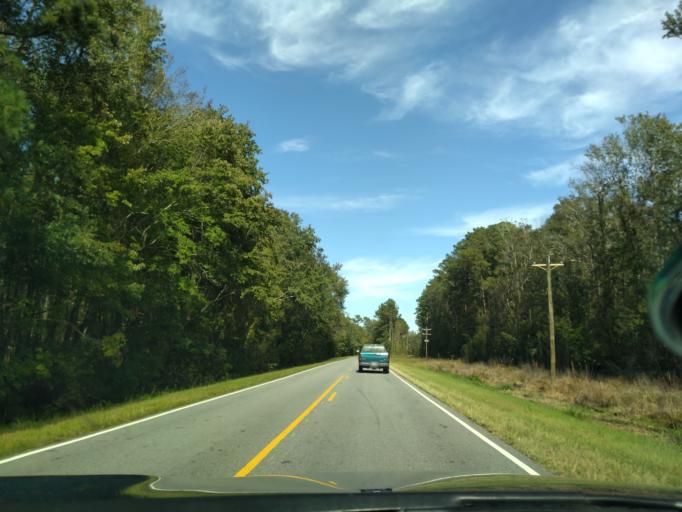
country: US
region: North Carolina
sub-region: Beaufort County
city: Belhaven
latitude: 35.6300
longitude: -76.6180
